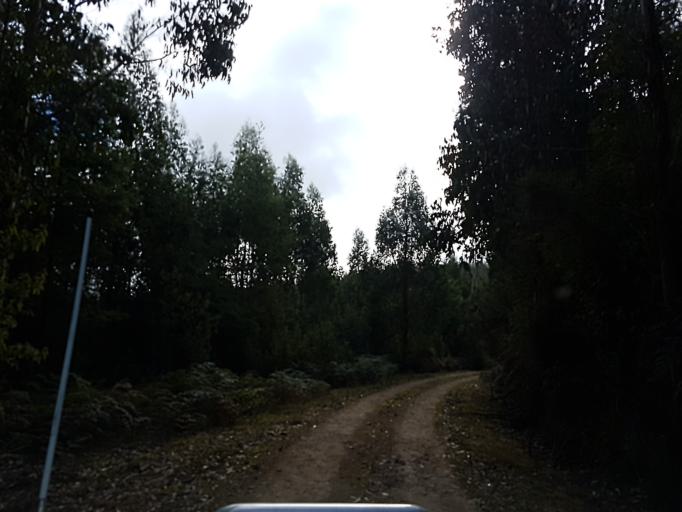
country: AU
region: Victoria
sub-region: Yarra Ranges
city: Millgrove
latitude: -37.5455
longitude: 145.7432
